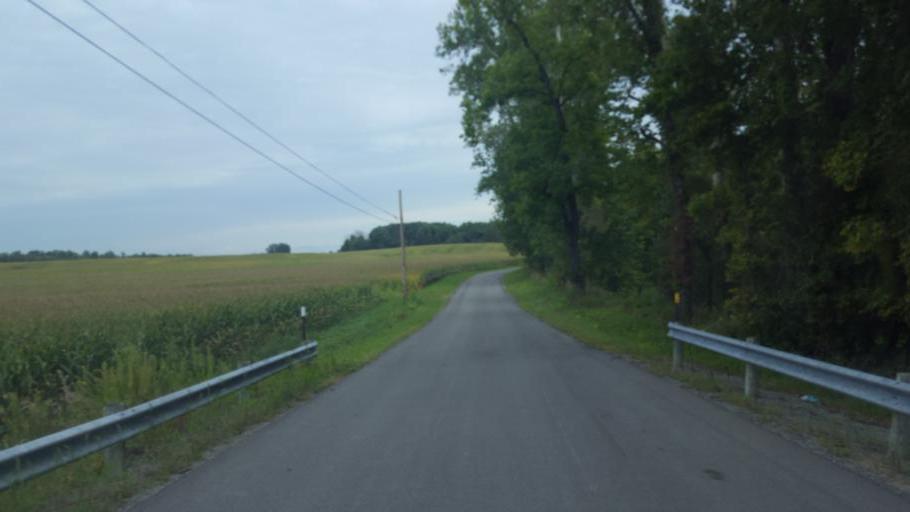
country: US
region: Ohio
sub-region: Wyandot County
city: Upper Sandusky
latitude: 40.7607
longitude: -83.1884
